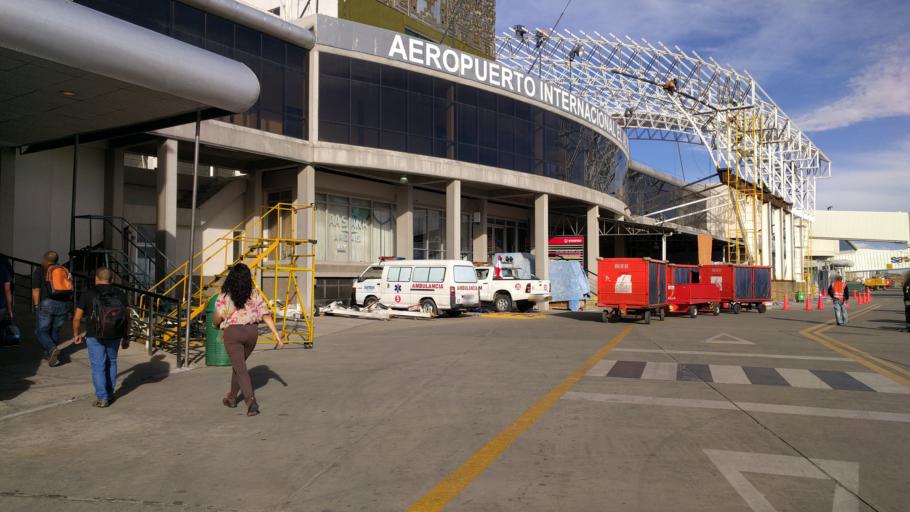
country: BO
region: La Paz
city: La Paz
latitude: -16.5091
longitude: -68.1775
